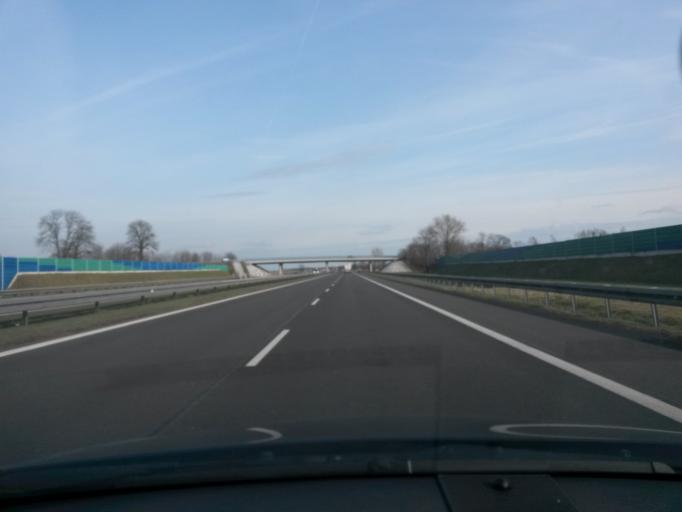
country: PL
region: Greater Poland Voivodeship
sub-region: Powiat slupecki
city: Ladek
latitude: 52.2376
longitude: 17.8870
